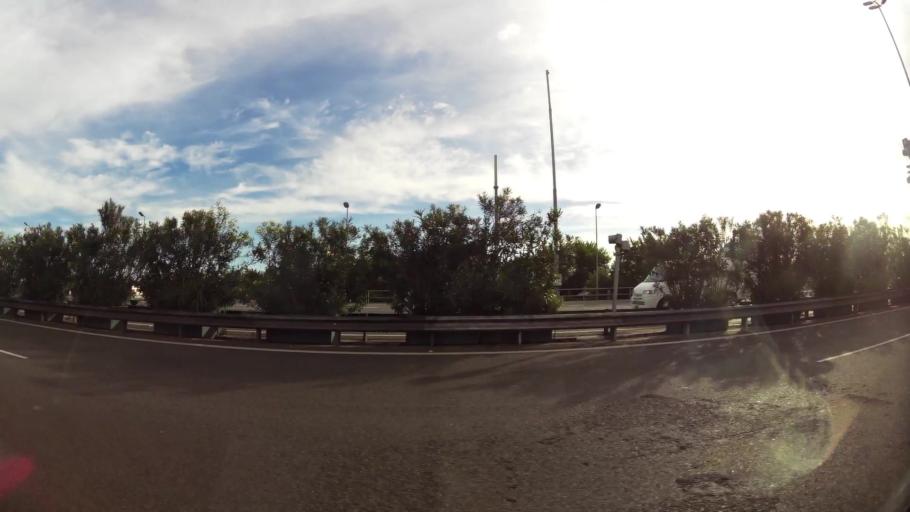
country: AR
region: Buenos Aires F.D.
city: Villa Santa Rita
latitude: -34.6445
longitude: -58.4878
